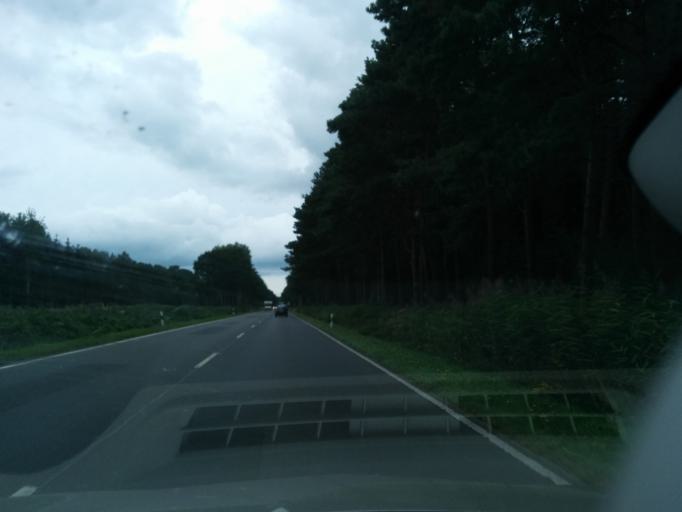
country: DE
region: Mecklenburg-Vorpommern
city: Koserow
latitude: 54.0554
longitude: 13.9886
